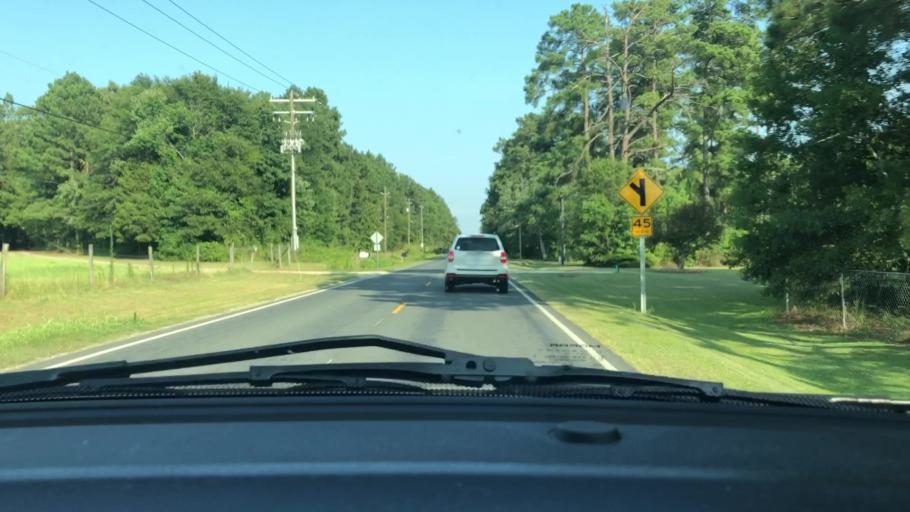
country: US
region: North Carolina
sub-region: Lee County
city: Broadway
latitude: 35.3617
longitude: -79.0878
